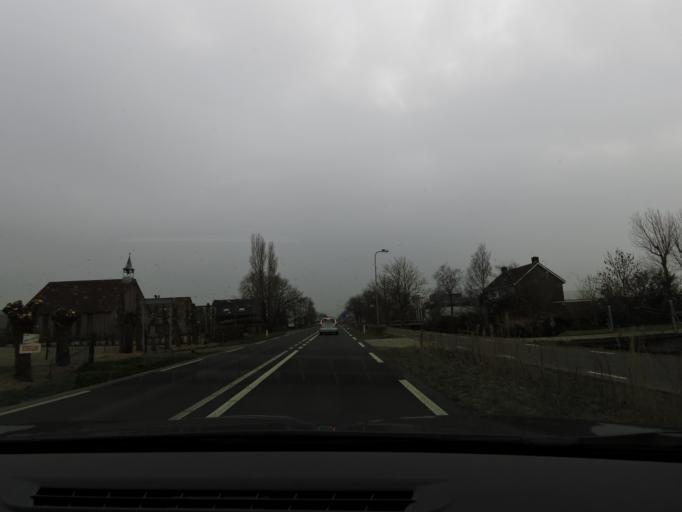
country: NL
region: South Holland
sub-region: Gemeente Nieuwkoop
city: Nieuwkoop
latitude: 52.1662
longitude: 4.7759
